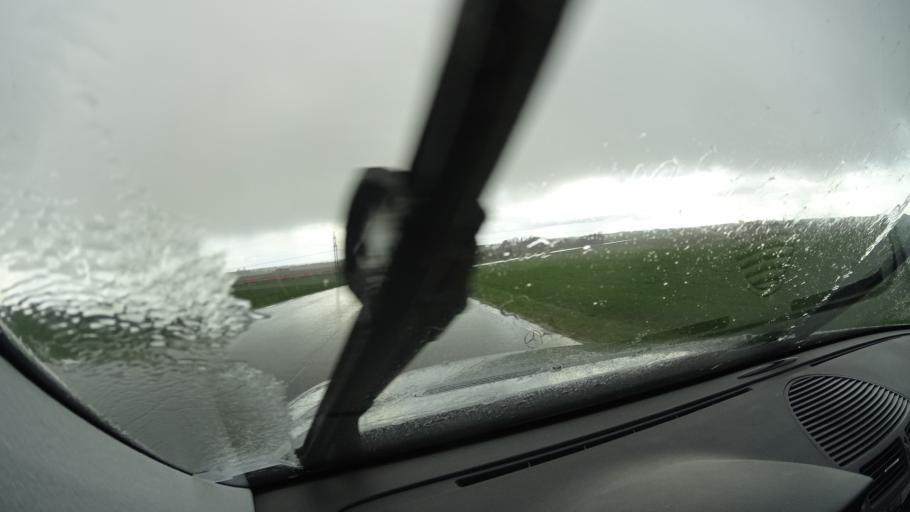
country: SE
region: Skane
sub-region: Lunds Kommun
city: Lund
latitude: 55.7666
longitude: 13.2224
